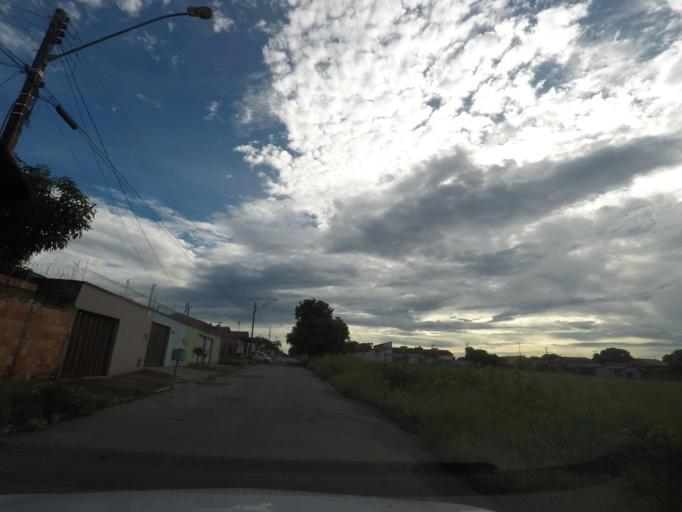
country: BR
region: Goias
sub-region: Aparecida De Goiania
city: Aparecida de Goiania
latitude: -16.7888
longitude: -49.3668
